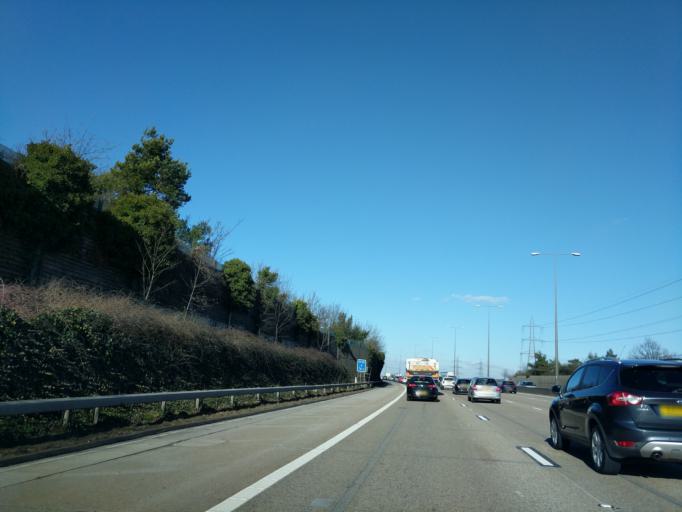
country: GB
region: England
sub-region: Surrey
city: Byfleet
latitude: 51.3459
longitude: -0.4855
